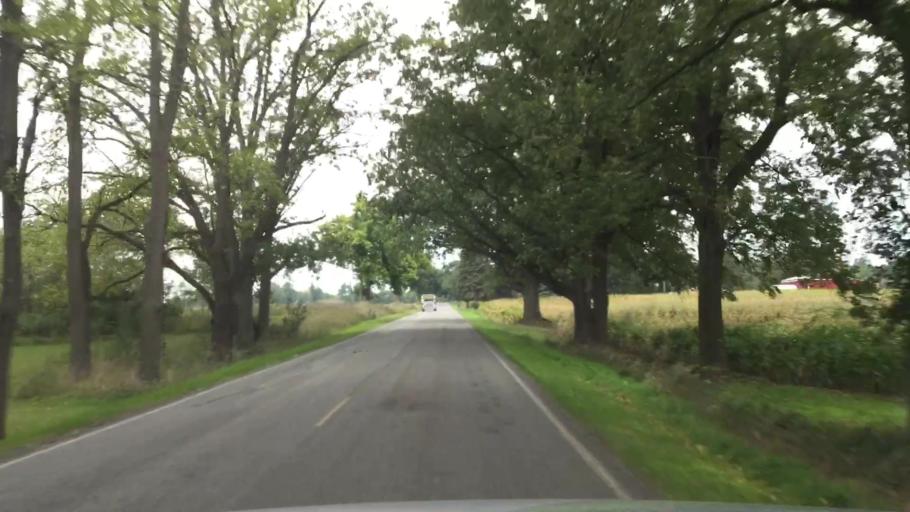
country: US
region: Michigan
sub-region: Shiawassee County
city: Perry
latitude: 42.8971
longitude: -84.1737
